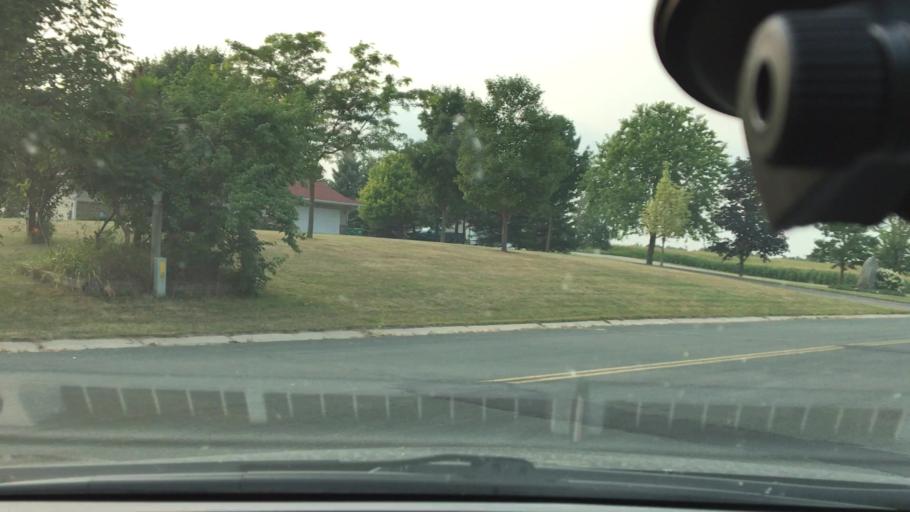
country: US
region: Minnesota
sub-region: Wright County
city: Albertville
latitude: 45.2855
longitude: -93.6839
